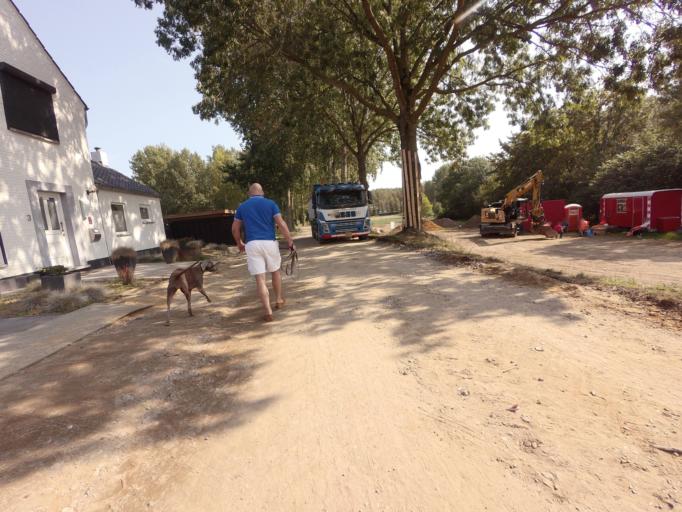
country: NL
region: Limburg
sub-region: Gemeente Maasgouw
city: Maasbracht
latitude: 51.1642
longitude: 5.8462
